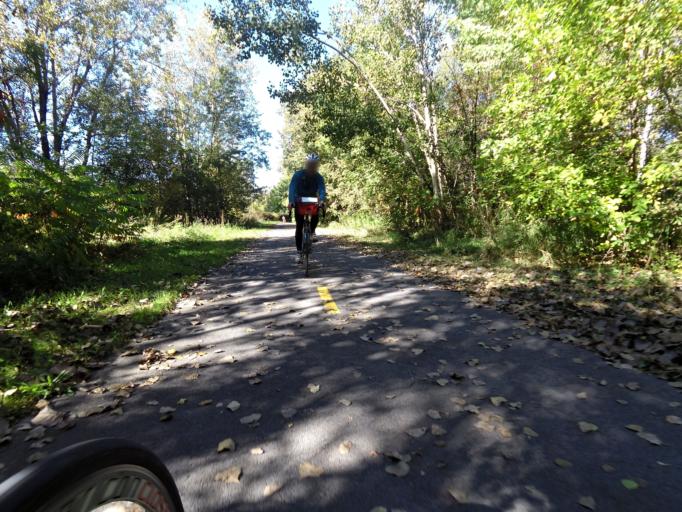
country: CA
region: Quebec
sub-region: Outaouais
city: Gatineau
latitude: 45.4769
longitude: -75.6482
